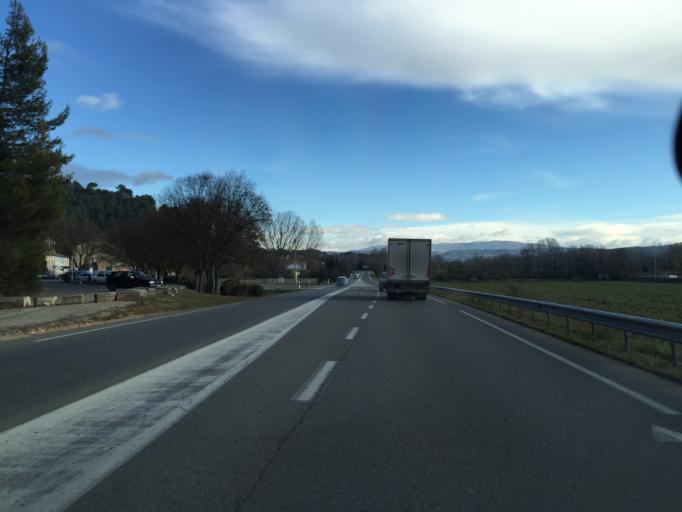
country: FR
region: Provence-Alpes-Cote d'Azur
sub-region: Departement du Vaucluse
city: Goult
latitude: 43.8590
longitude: 5.2290
